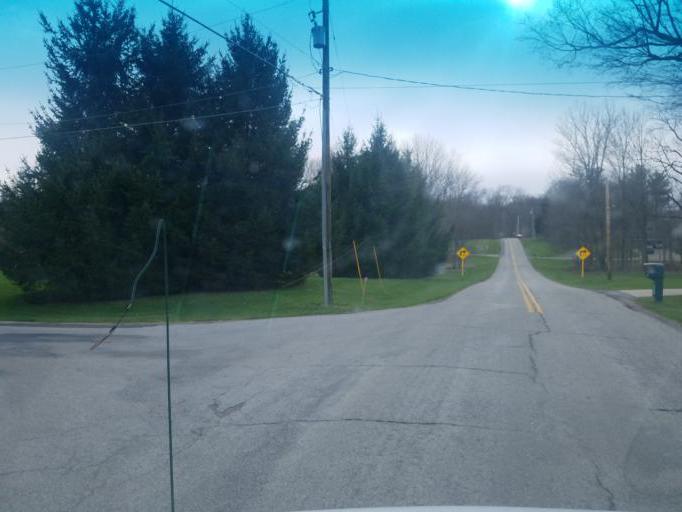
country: US
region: Ohio
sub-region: Richland County
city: Ontario
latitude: 40.7357
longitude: -82.6051
